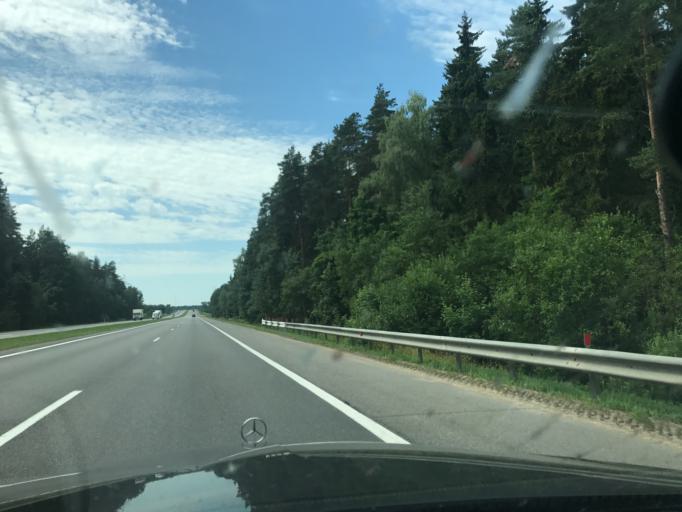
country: BY
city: Michanovichi
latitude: 53.7695
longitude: 27.6852
